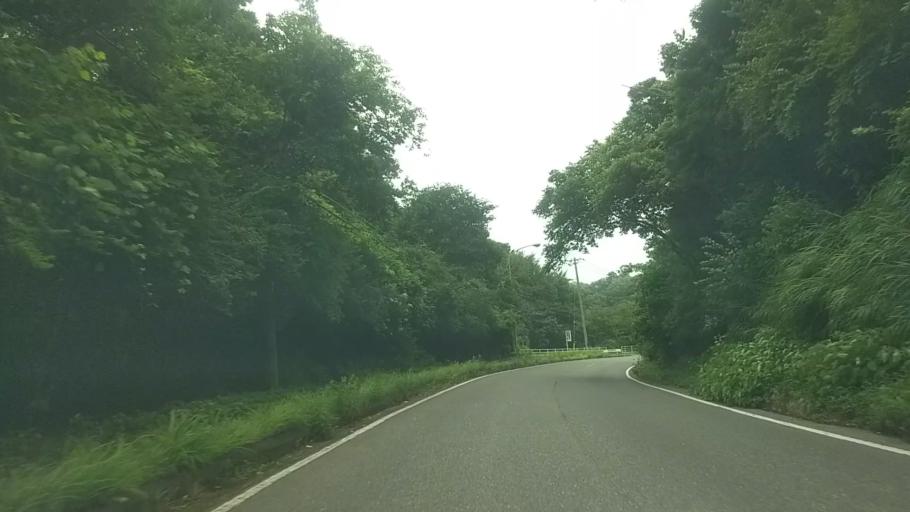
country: JP
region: Chiba
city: Kawaguchi
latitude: 35.2421
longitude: 140.0354
